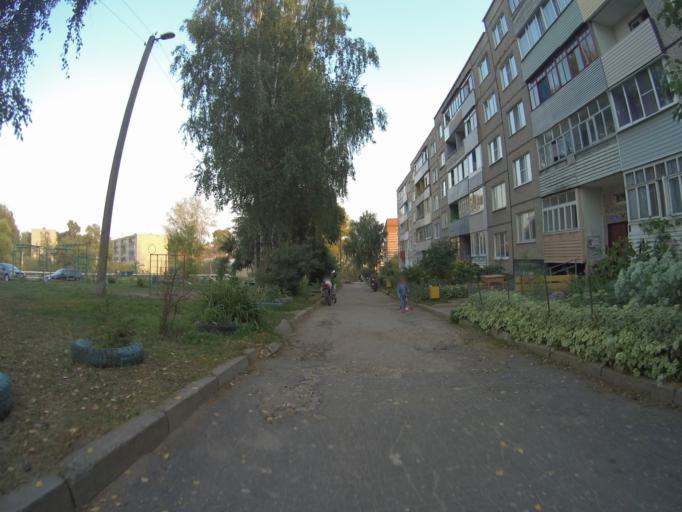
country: RU
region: Vladimir
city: Orgtrud
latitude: 56.1811
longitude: 40.6069
